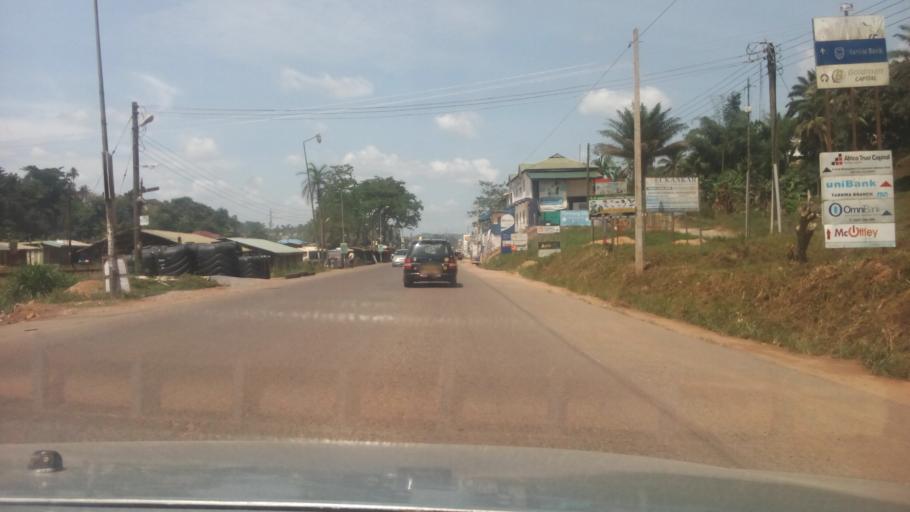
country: GH
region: Western
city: Tarkwa
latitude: 5.3010
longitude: -1.9972
